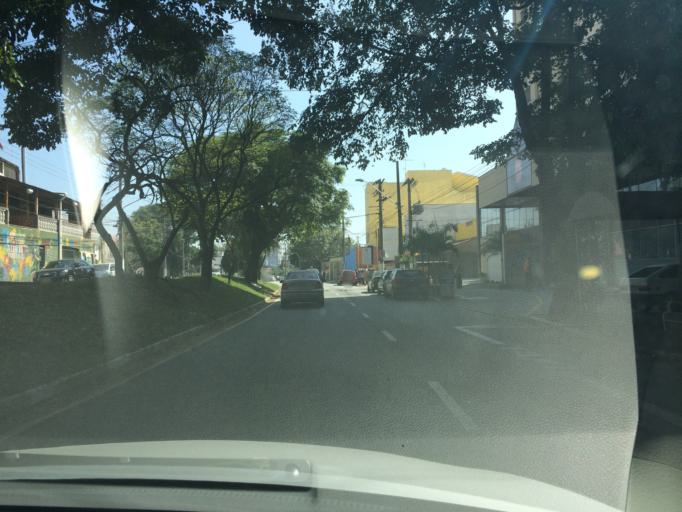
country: BR
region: Sao Paulo
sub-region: Guarulhos
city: Guarulhos
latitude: -23.4556
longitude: -46.5338
